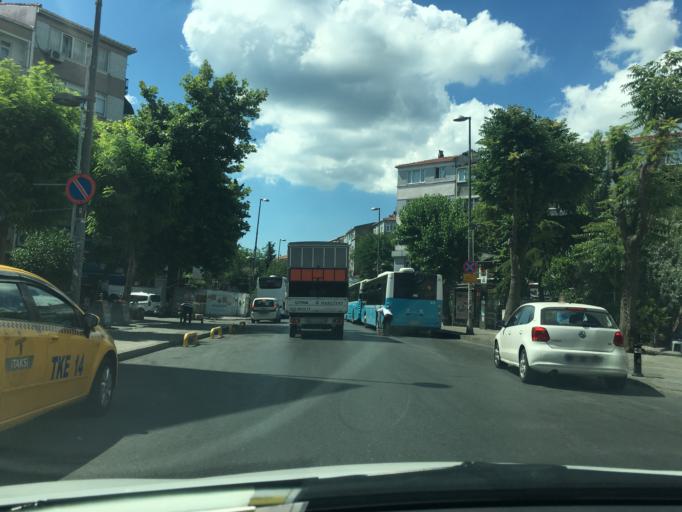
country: TR
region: Istanbul
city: Istanbul
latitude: 41.0056
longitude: 28.9312
